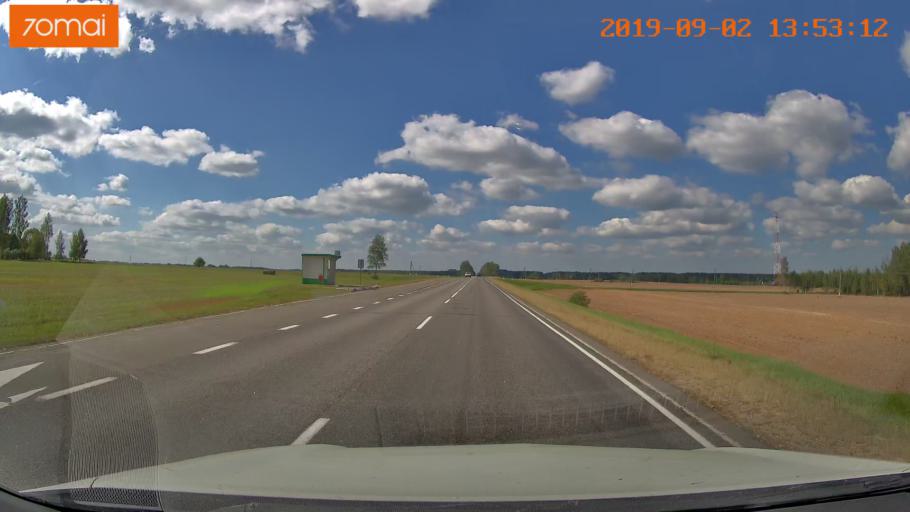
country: BY
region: Mogilev
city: Cherykaw
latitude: 53.6689
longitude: 31.2209
